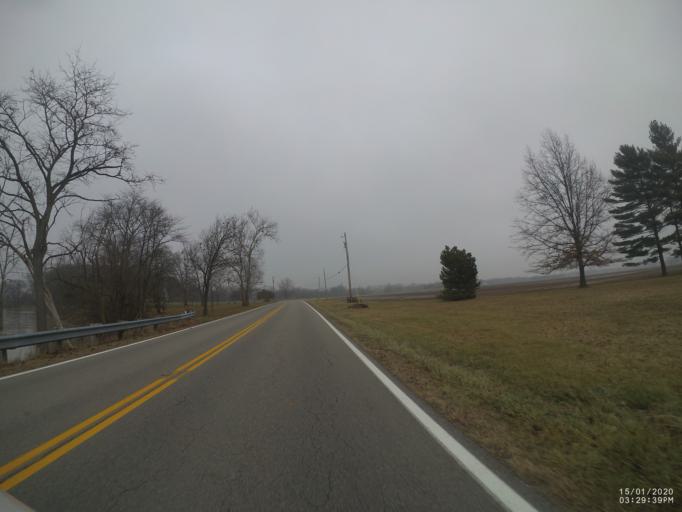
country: US
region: Ohio
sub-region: Sandusky County
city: Woodville
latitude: 41.4416
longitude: -83.3855
